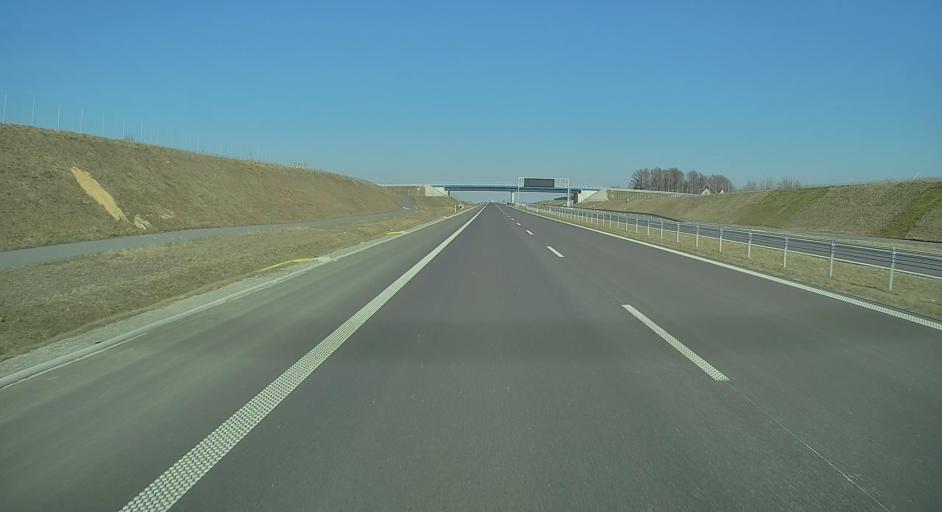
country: PL
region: Lublin Voivodeship
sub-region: Powiat krasnicki
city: Szastarka
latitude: 50.8235
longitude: 22.2989
